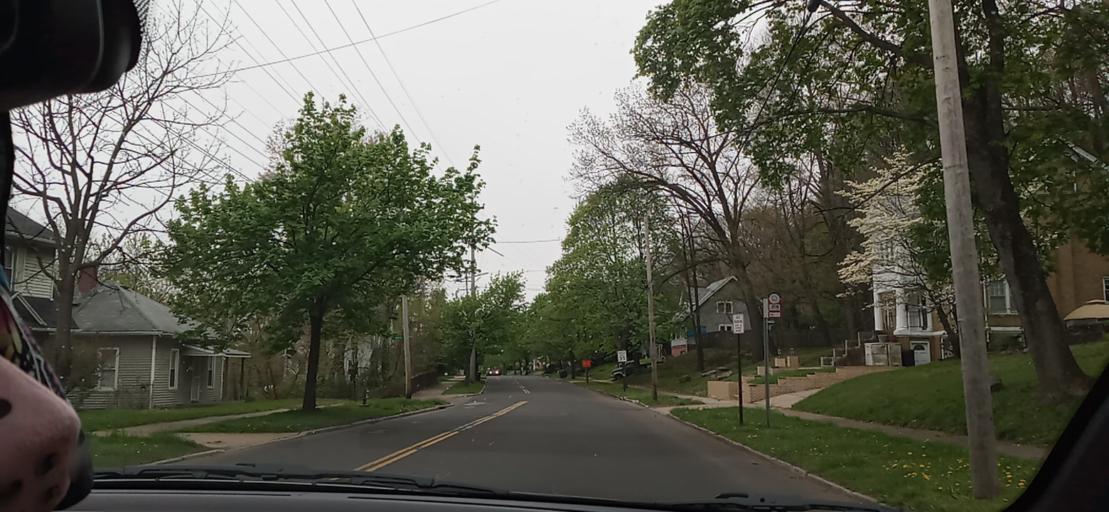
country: US
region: Ohio
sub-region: Summit County
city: Akron
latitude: 41.0571
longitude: -81.5501
